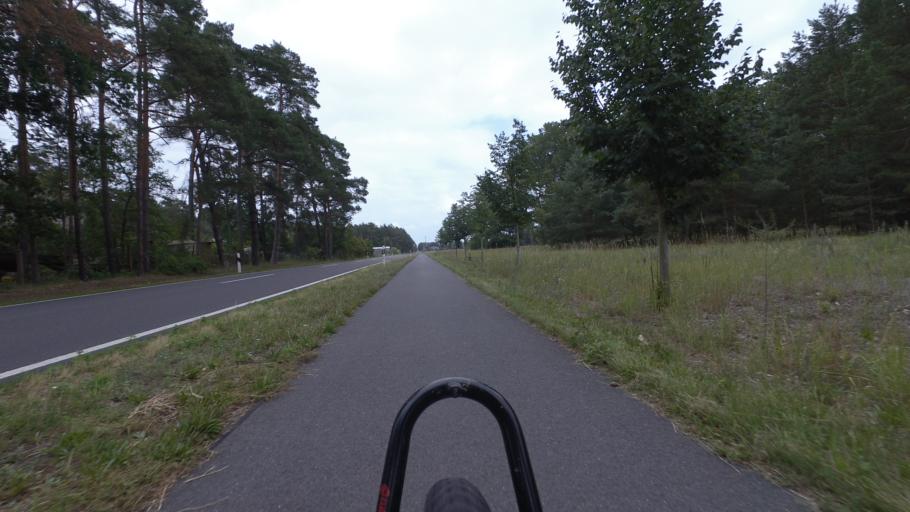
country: DE
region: Brandenburg
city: Sperenberg
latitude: 52.0832
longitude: 13.3069
